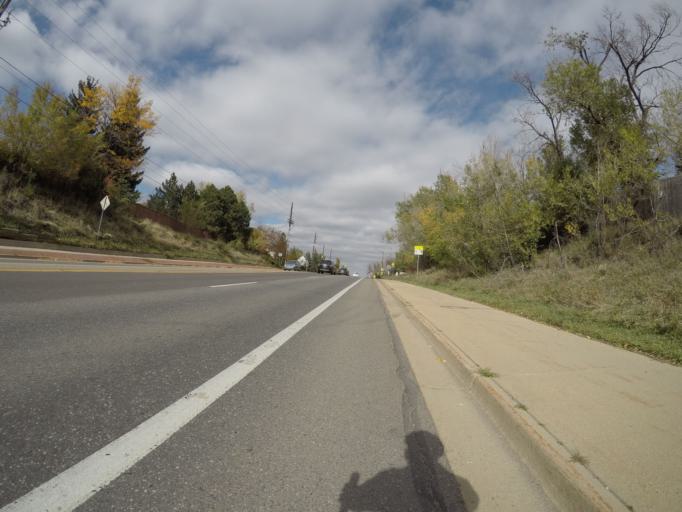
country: US
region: Colorado
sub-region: Boulder County
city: Boulder
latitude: 40.0429
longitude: -105.2820
